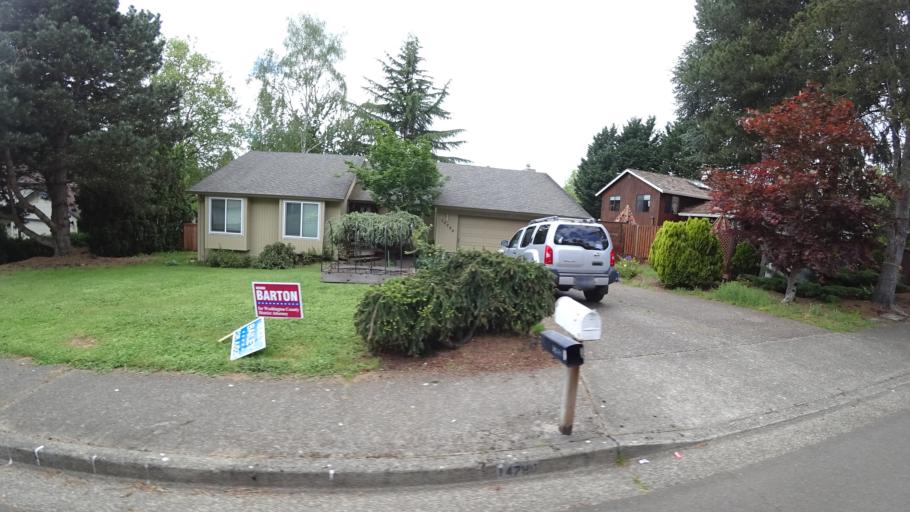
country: US
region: Oregon
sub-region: Washington County
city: Beaverton
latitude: 45.4733
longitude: -122.8292
